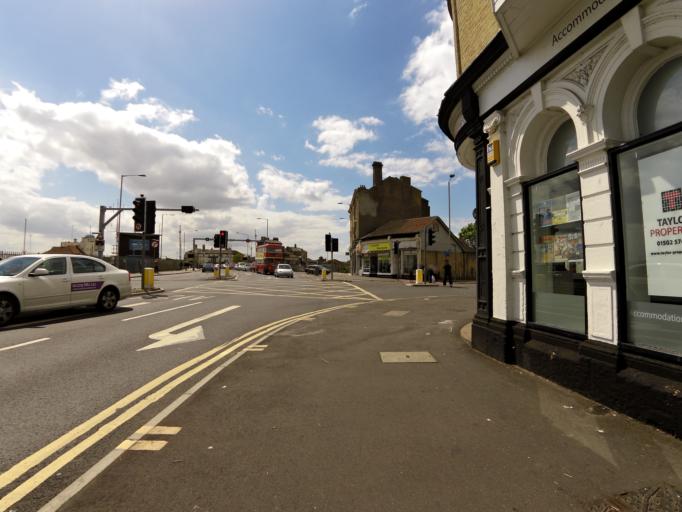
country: GB
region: England
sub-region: Suffolk
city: Lowestoft
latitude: 52.4738
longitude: 1.7503
